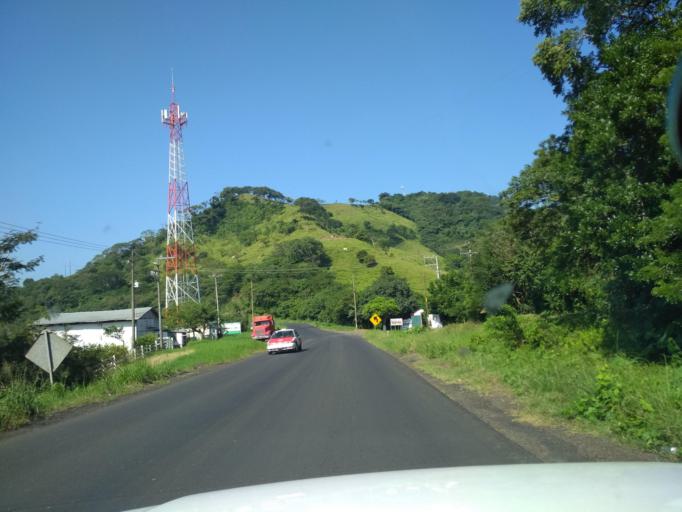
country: MX
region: Veracruz
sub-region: San Andres Tuxtla
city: Texcaltitan Xoteapan (Texcaltitan)
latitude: 18.4434
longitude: -95.2502
